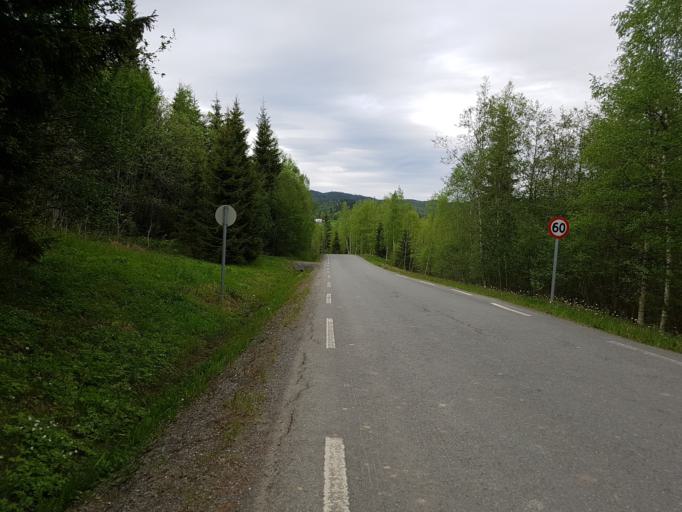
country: NO
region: Nord-Trondelag
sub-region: Levanger
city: Skogn
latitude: 63.6287
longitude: 11.2763
